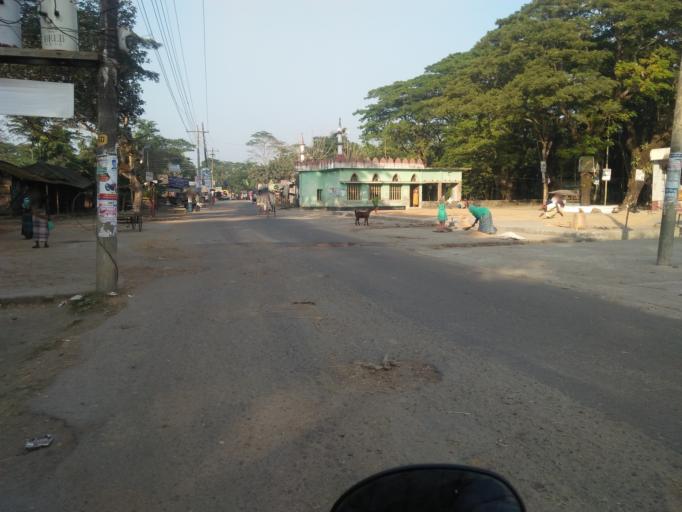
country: BD
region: Barisal
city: Bhola
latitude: 22.7499
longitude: 90.6348
